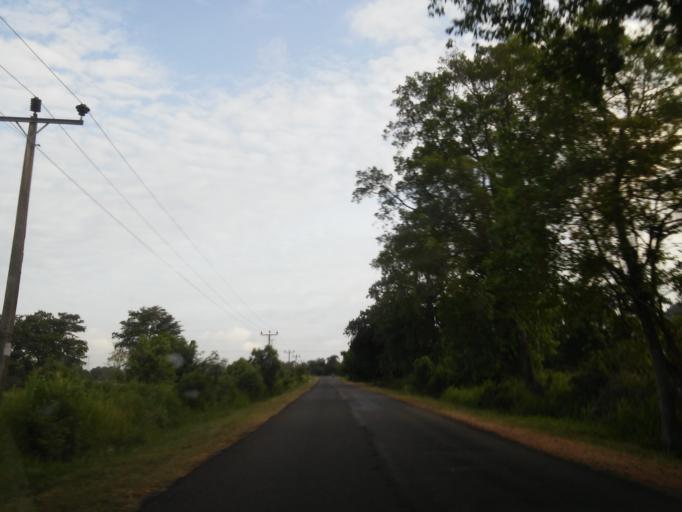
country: LK
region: Central
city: Sigiriya
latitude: 8.0916
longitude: 80.6370
